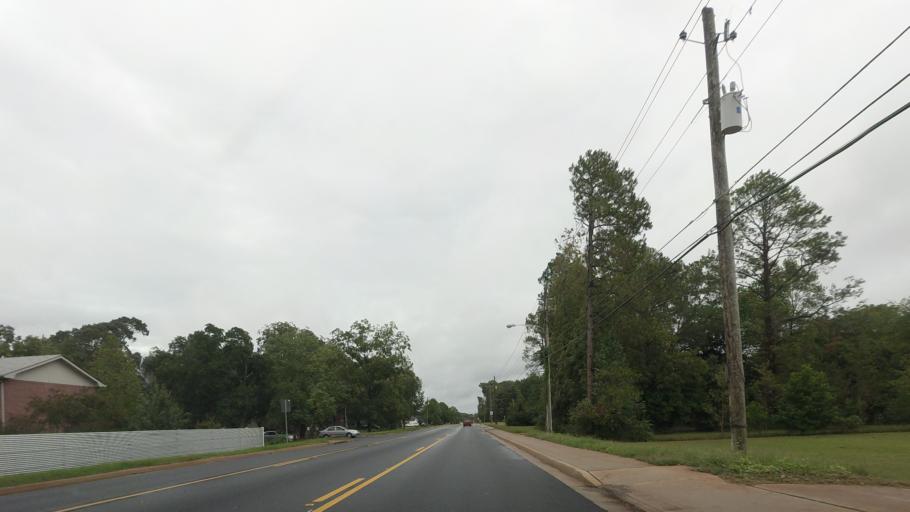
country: US
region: Georgia
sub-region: Houston County
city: Warner Robins
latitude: 32.5748
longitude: -83.6321
